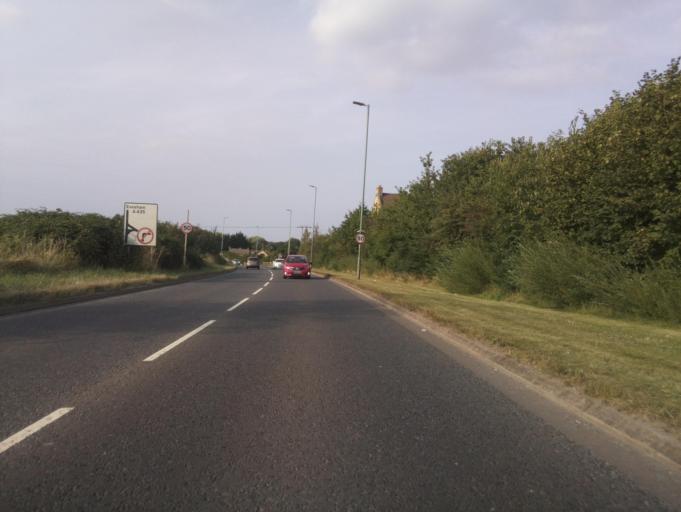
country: GB
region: England
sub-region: Gloucestershire
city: Gotherington
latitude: 51.9535
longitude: -2.0664
